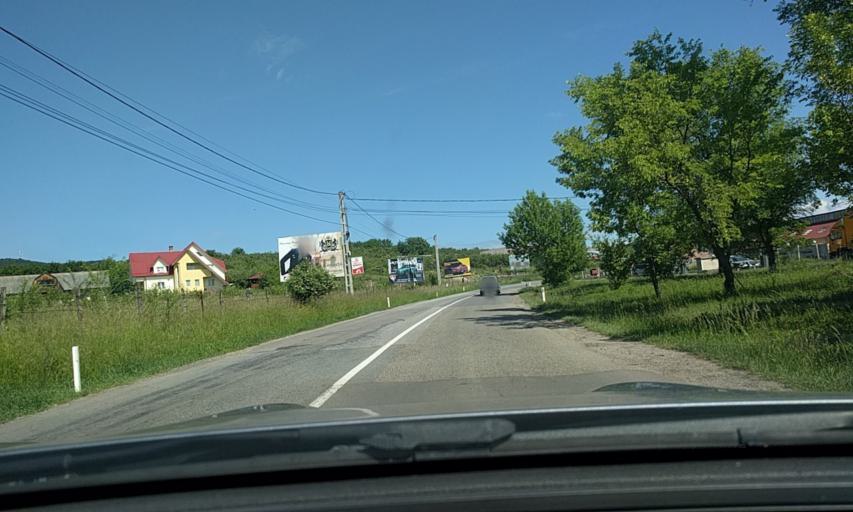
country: RO
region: Bistrita-Nasaud
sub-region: Municipiul Bistrita
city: Unirea
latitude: 47.1553
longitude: 24.5088
